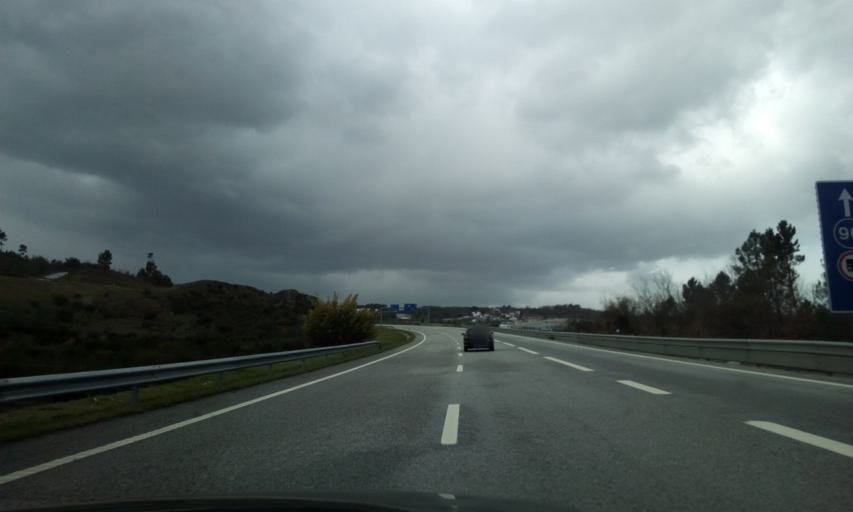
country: PT
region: Viseu
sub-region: Viseu
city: Rio de Loba
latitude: 40.6333
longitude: -7.8280
